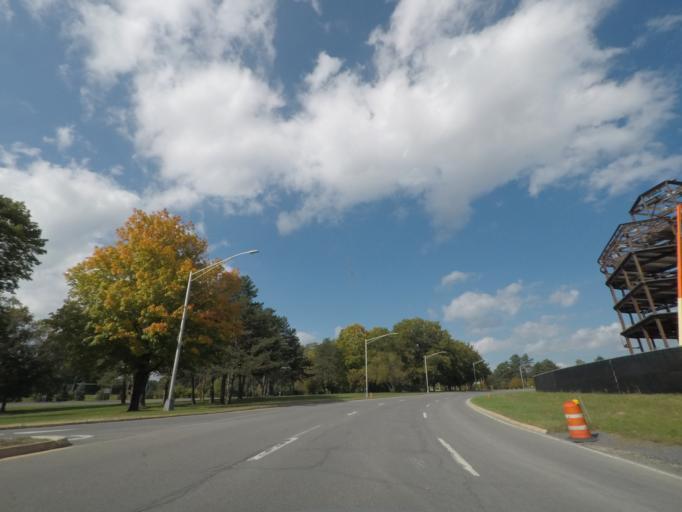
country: US
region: New York
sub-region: Albany County
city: Roessleville
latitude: 42.6796
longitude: -73.8164
